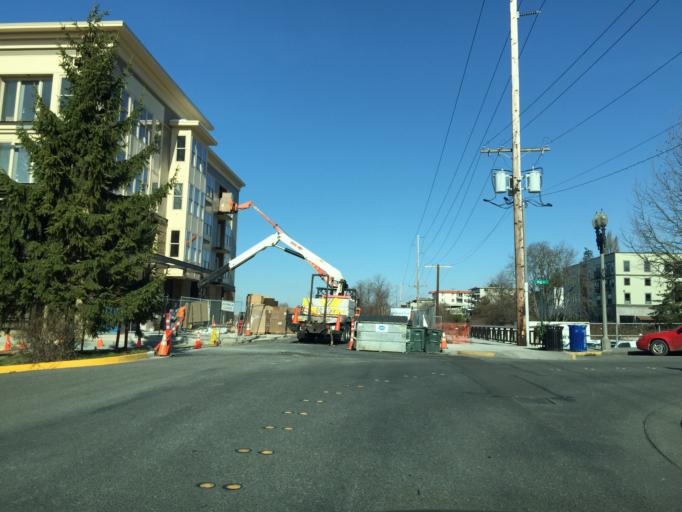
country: US
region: Washington
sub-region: Whatcom County
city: Bellingham
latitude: 48.7208
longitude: -122.5046
